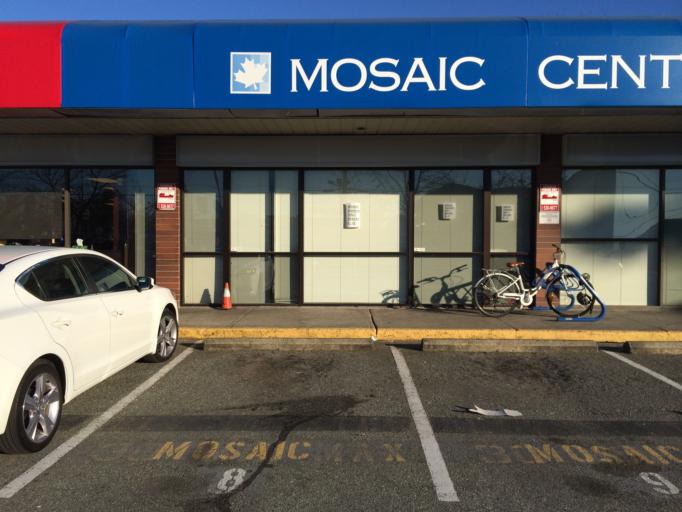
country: CA
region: British Columbia
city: Burnaby
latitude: 49.2209
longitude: -122.9772
